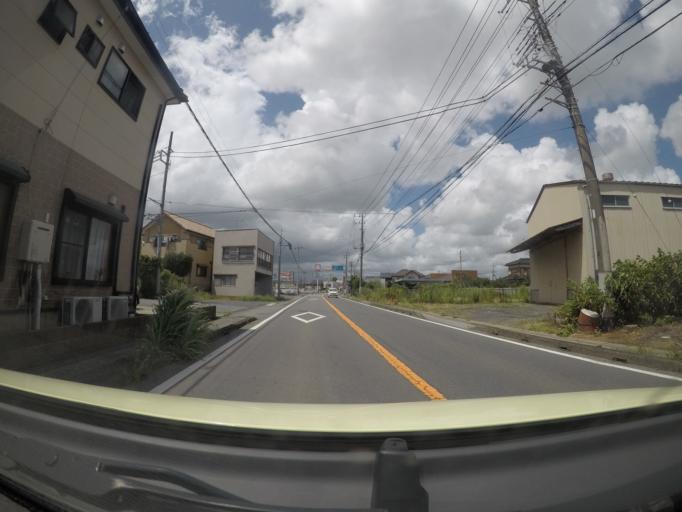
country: JP
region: Ibaraki
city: Mitsukaido
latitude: 36.0323
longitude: 139.9888
